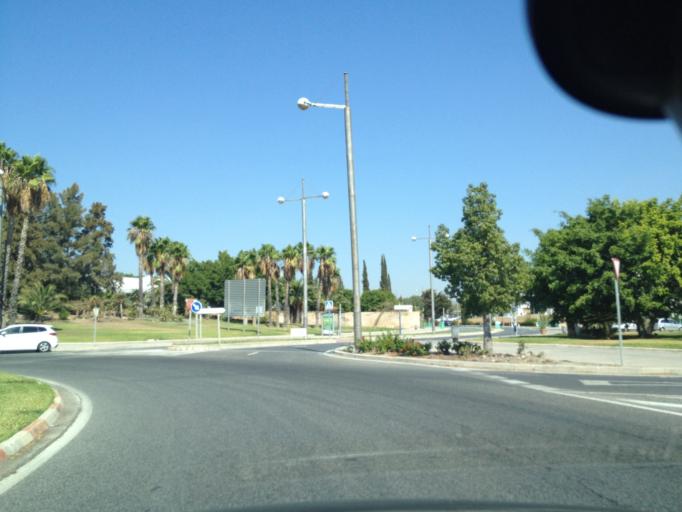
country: ES
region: Andalusia
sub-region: Provincia de Malaga
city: Estacion de Cartama
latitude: 36.7312
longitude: -4.5503
